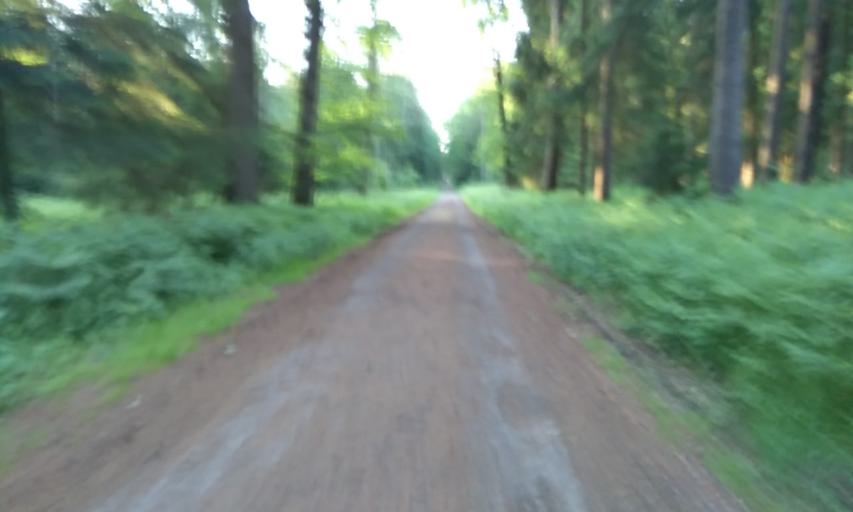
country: DE
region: Lower Saxony
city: Dollern
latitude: 53.5220
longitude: 9.5158
